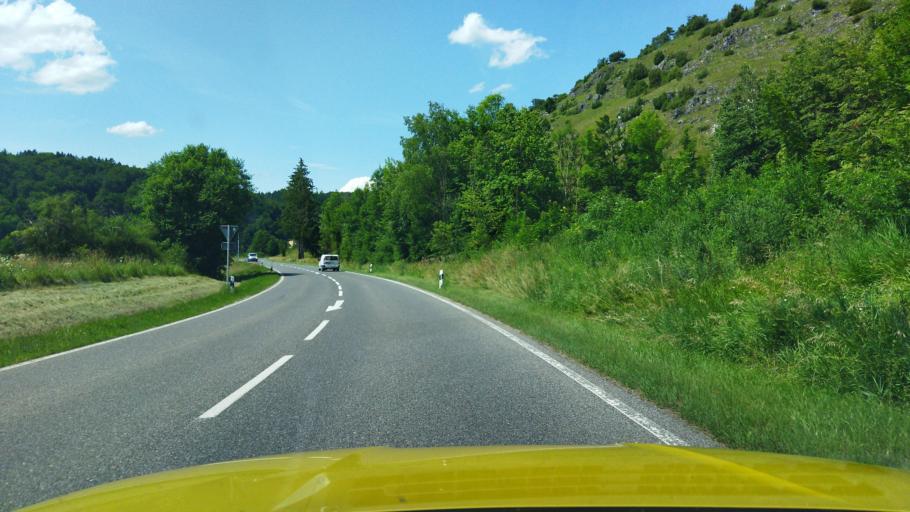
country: DE
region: Bavaria
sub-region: Lower Bavaria
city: Riedenburg
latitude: 48.9478
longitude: 11.6870
